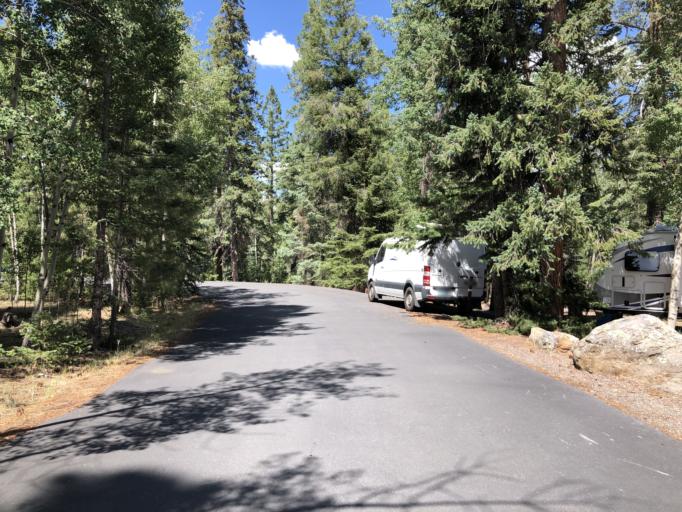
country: US
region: Arizona
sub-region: Apache County
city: Eagar
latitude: 33.8778
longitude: -109.3997
